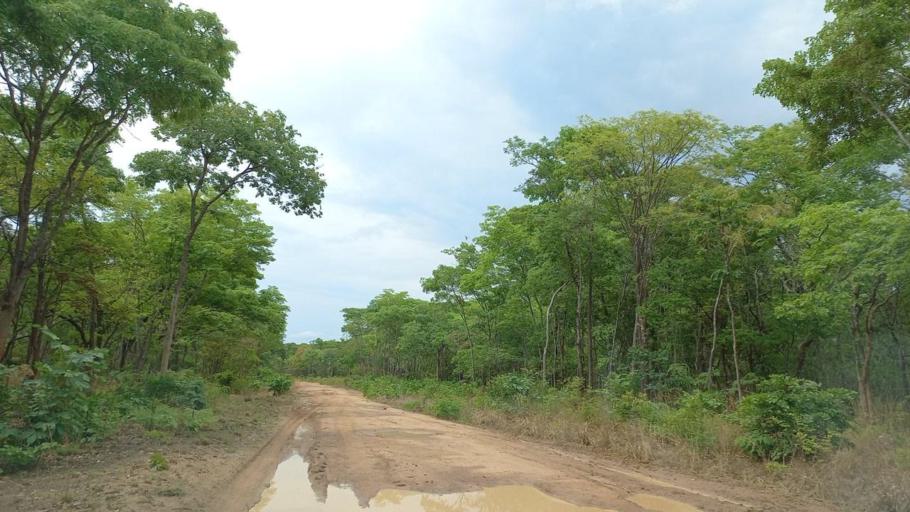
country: ZM
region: North-Western
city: Kalengwa
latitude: -13.5684
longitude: 24.9709
